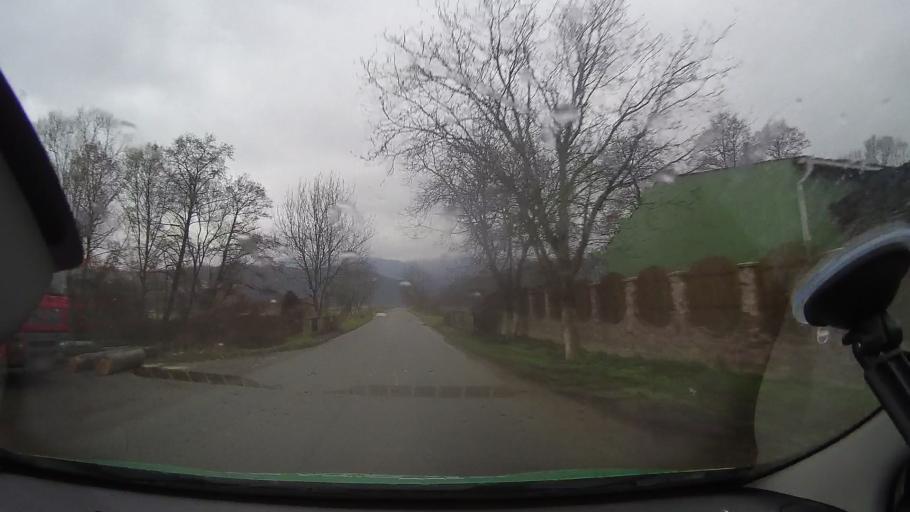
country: RO
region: Hunedoara
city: Vata de Jos
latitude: 46.1874
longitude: 22.6064
